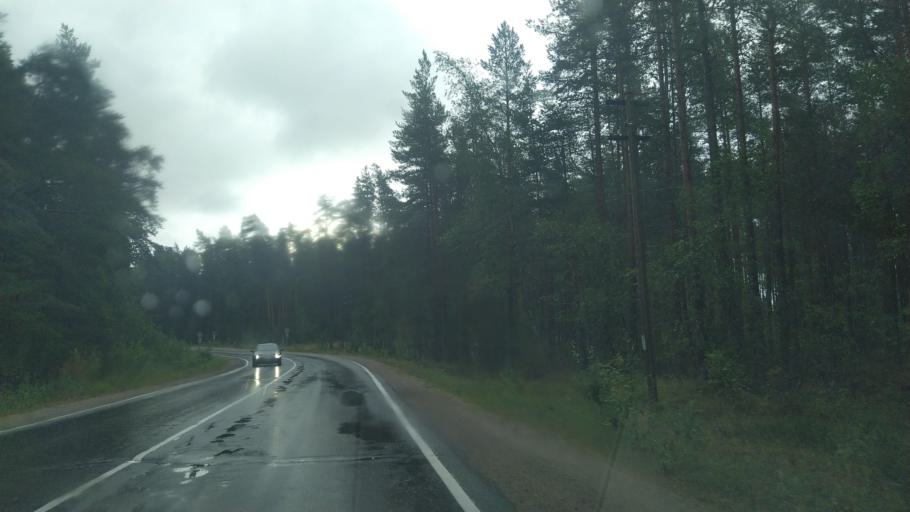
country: RU
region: Leningrad
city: Priozersk
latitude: 61.0016
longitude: 30.1983
